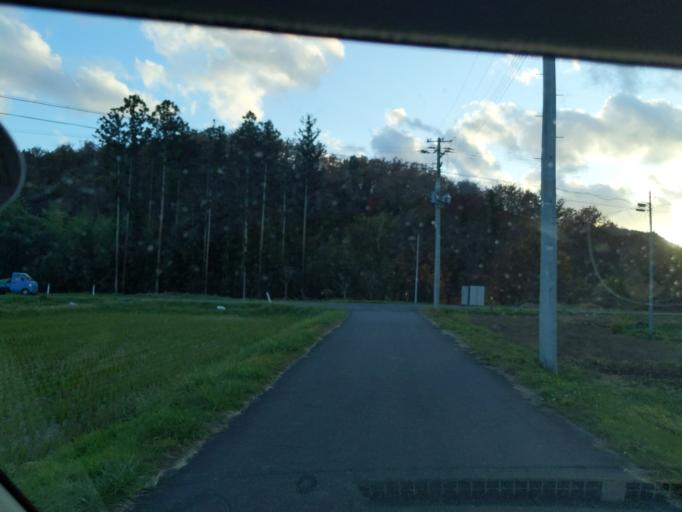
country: JP
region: Iwate
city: Mizusawa
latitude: 39.0436
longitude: 141.0480
